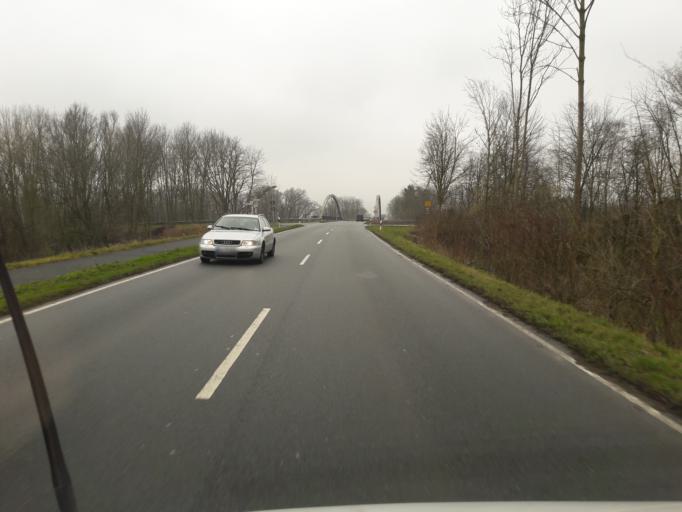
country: DE
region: North Rhine-Westphalia
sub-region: Regierungsbezirk Detmold
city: Hille
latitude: 52.3108
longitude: 8.8189
